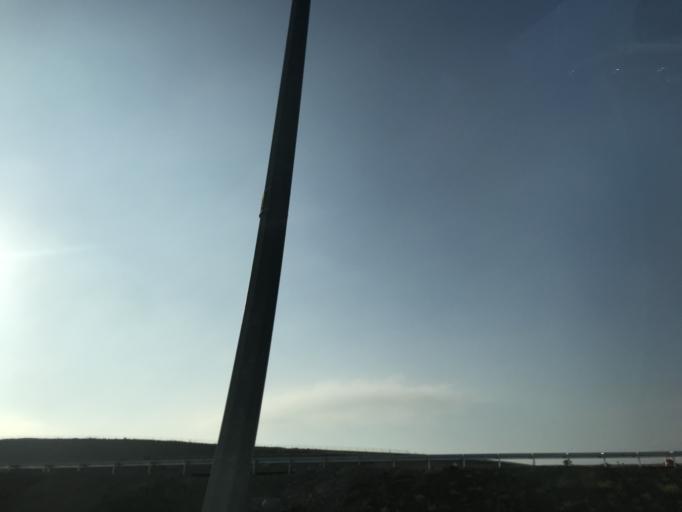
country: TR
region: Balikesir
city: Gobel
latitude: 40.0401
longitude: 28.2195
